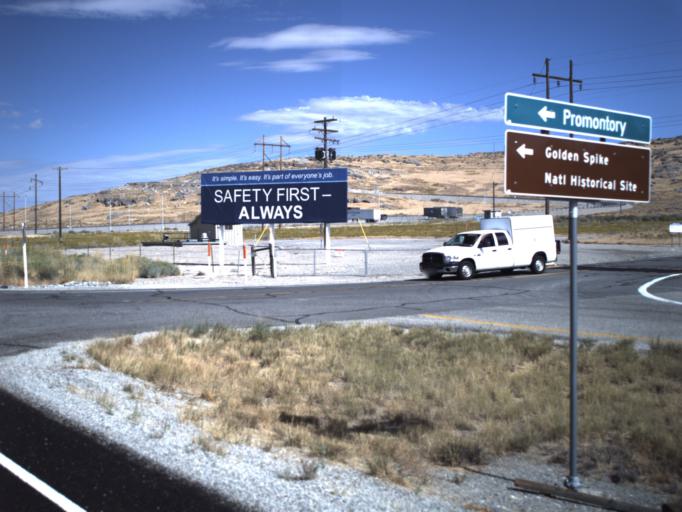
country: US
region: Utah
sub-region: Box Elder County
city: Tremonton
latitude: 41.6363
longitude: -112.4235
